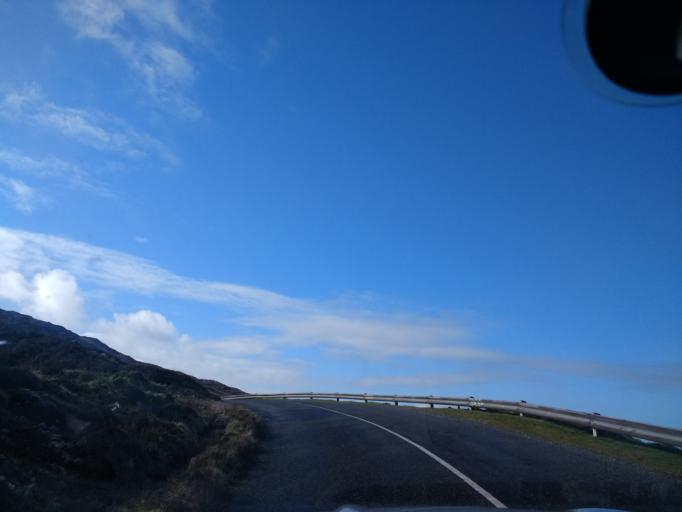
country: IE
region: Ulster
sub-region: County Donegal
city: Buncrana
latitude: 55.1823
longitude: -7.5801
